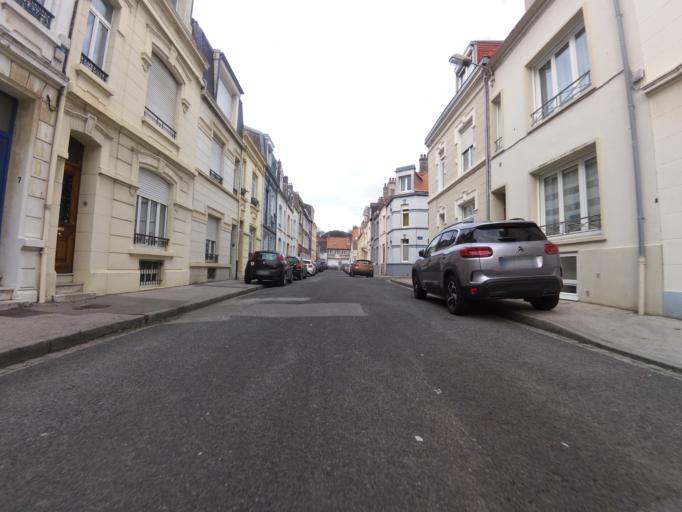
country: FR
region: Nord-Pas-de-Calais
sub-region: Departement du Pas-de-Calais
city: Saint-Martin-Boulogne
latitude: 50.7264
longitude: 1.6183
